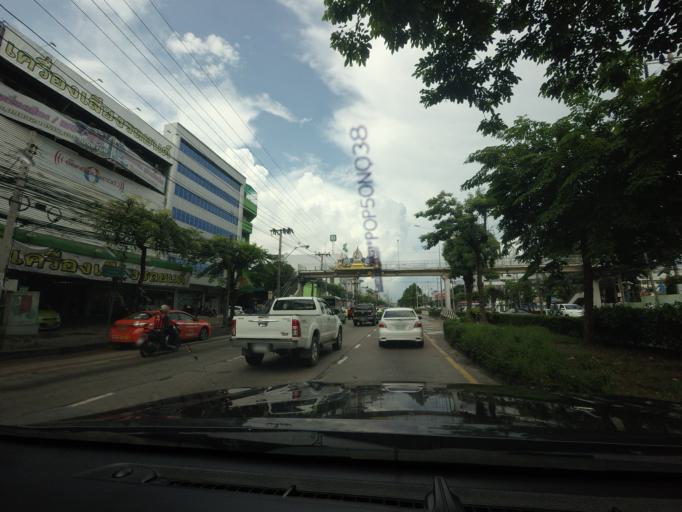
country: TH
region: Bangkok
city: Bang Khae
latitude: 13.7101
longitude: 100.4010
